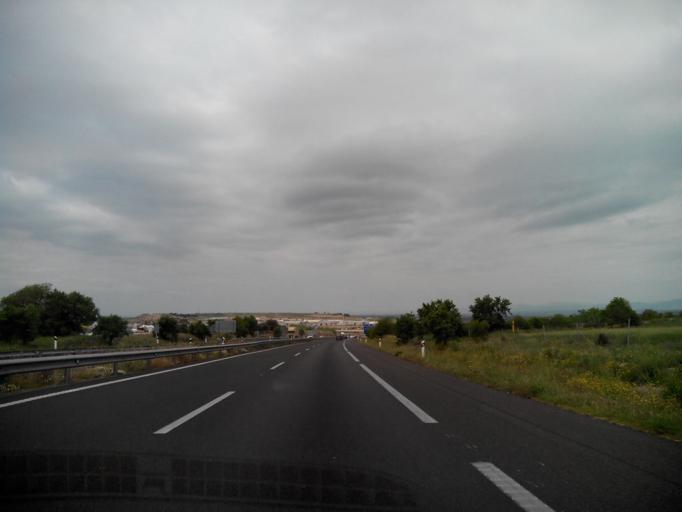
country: ES
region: Catalonia
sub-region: Provincia de Lleida
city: Tarrega
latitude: 41.6585
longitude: 1.1581
